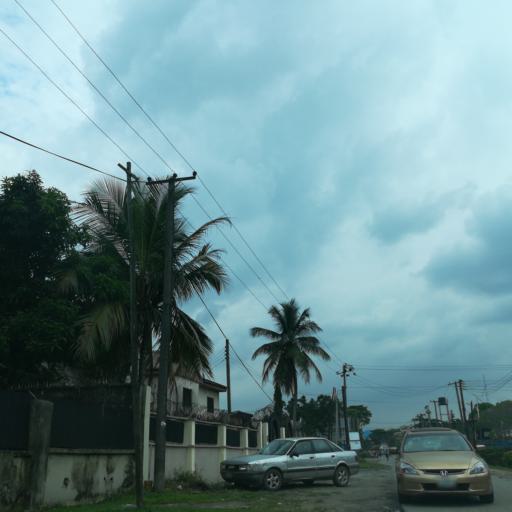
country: NG
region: Rivers
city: Port Harcourt
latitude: 4.8294
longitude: 6.9948
